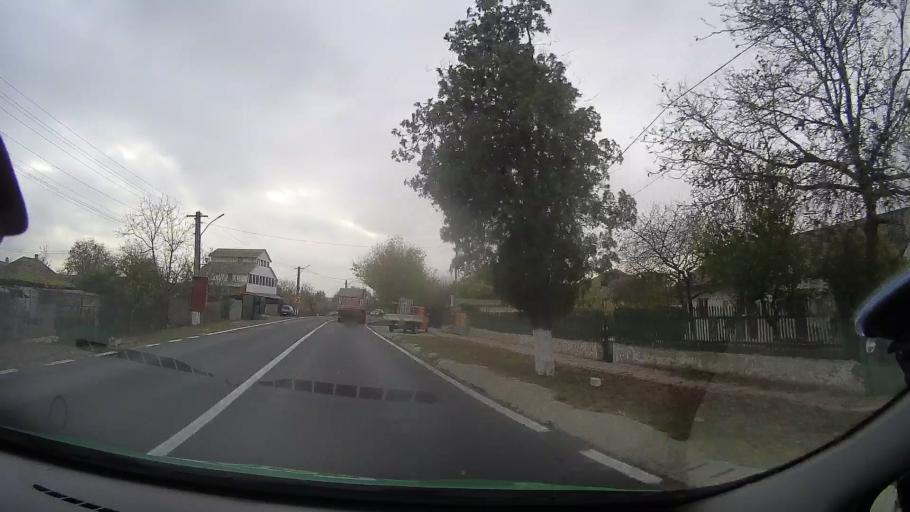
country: RO
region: Constanta
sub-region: Comuna Castelu
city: Castelu
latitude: 44.2532
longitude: 28.3320
